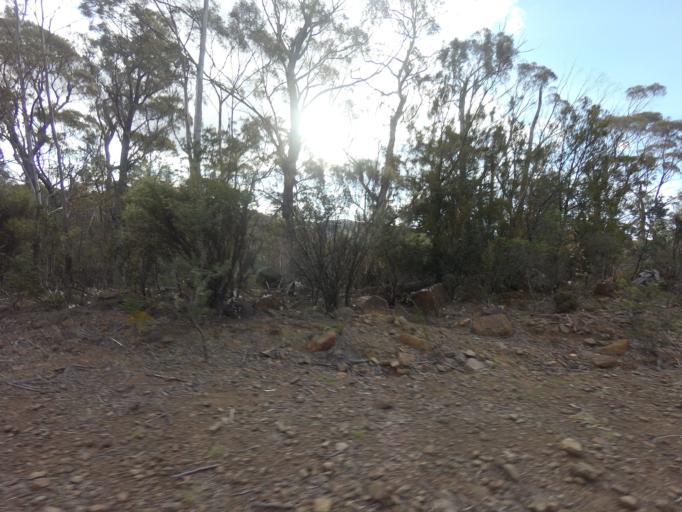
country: AU
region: Tasmania
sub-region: Break O'Day
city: St Helens
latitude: -41.8613
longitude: 148.0236
